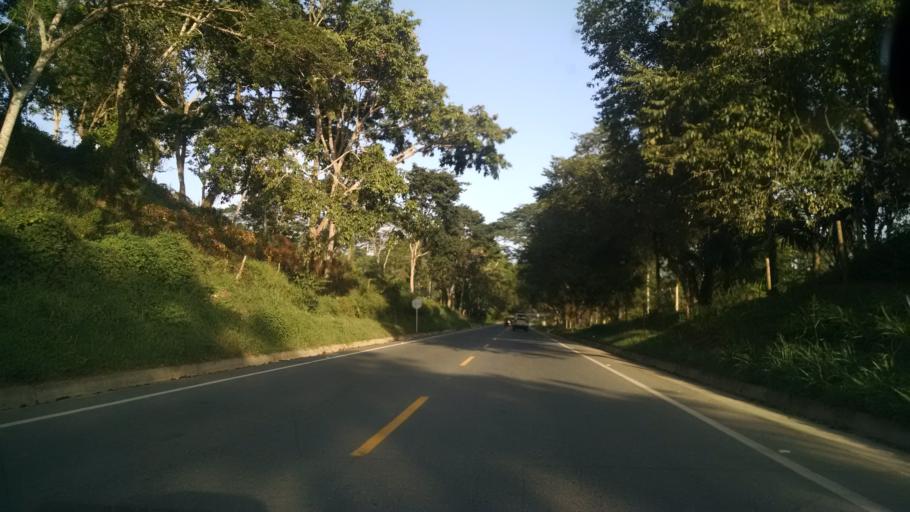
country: CO
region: Cordoba
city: Canalete
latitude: 8.8470
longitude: -76.1403
